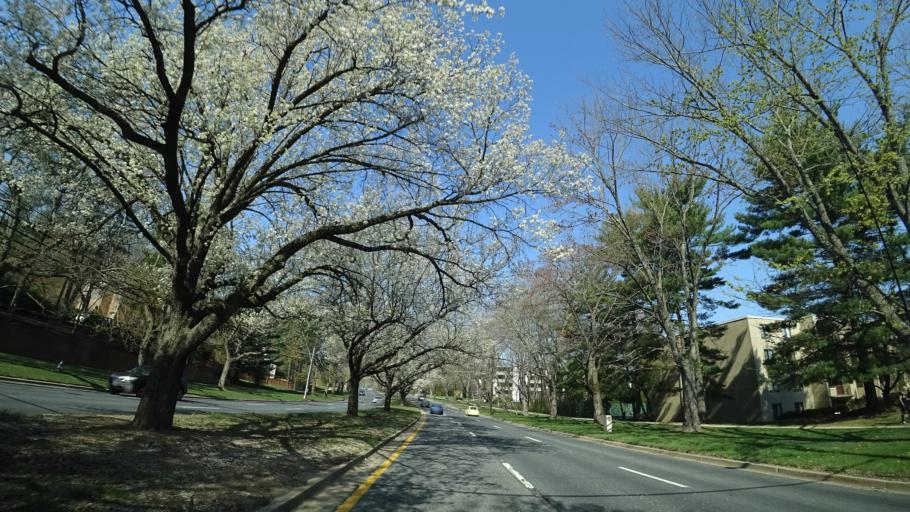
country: US
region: Maryland
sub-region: Montgomery County
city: North Bethesda
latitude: 39.0230
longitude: -77.1519
